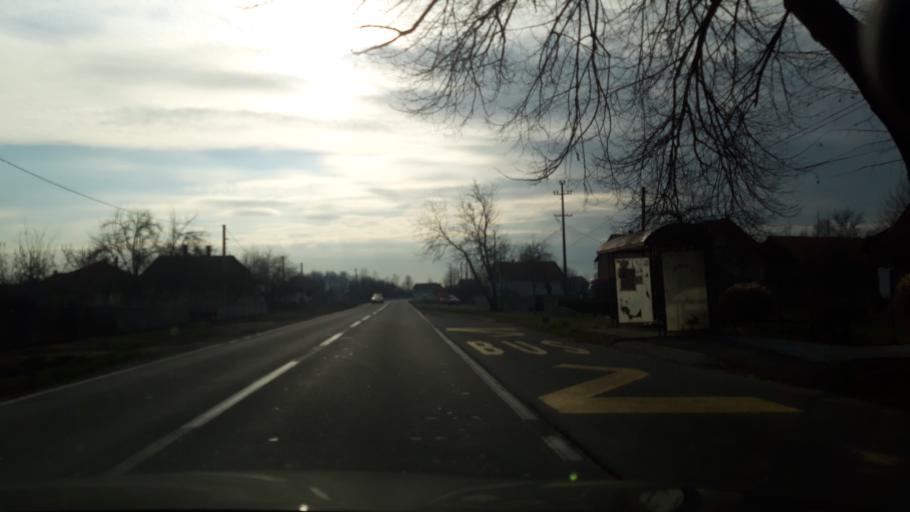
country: RS
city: Lipnicki Sor
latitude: 44.5942
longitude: 19.2574
